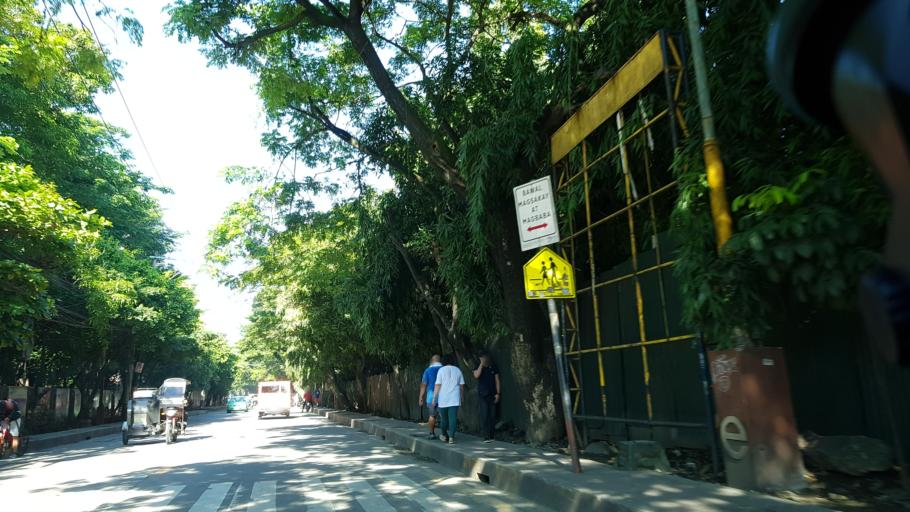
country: PH
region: Calabarzon
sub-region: Province of Rizal
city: Cainta
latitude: 14.5756
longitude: 121.0977
